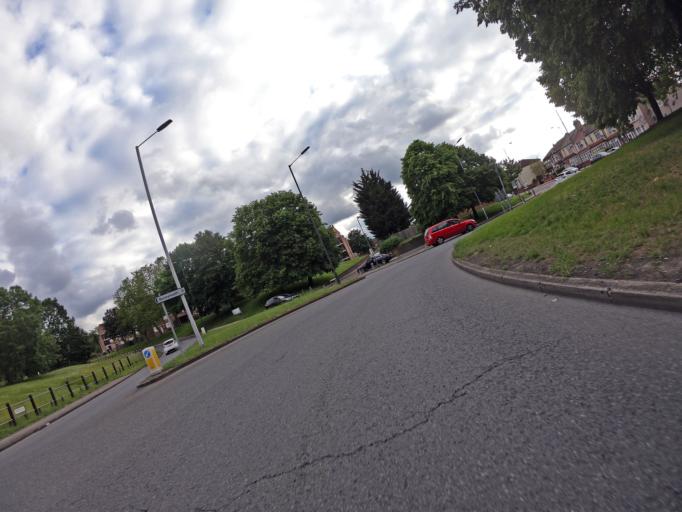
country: GB
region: England
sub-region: Greater London
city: Abbey Wood
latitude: 51.4886
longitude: 0.1219
